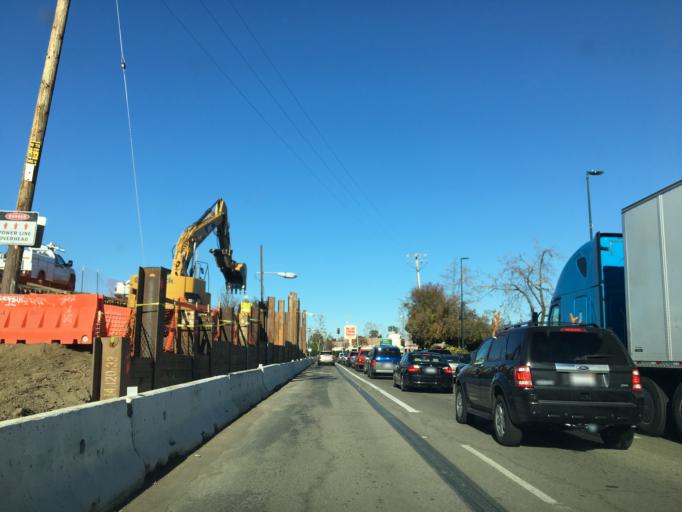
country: US
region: California
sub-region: Santa Clara County
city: Cupertino
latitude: 37.3219
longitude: -121.9953
